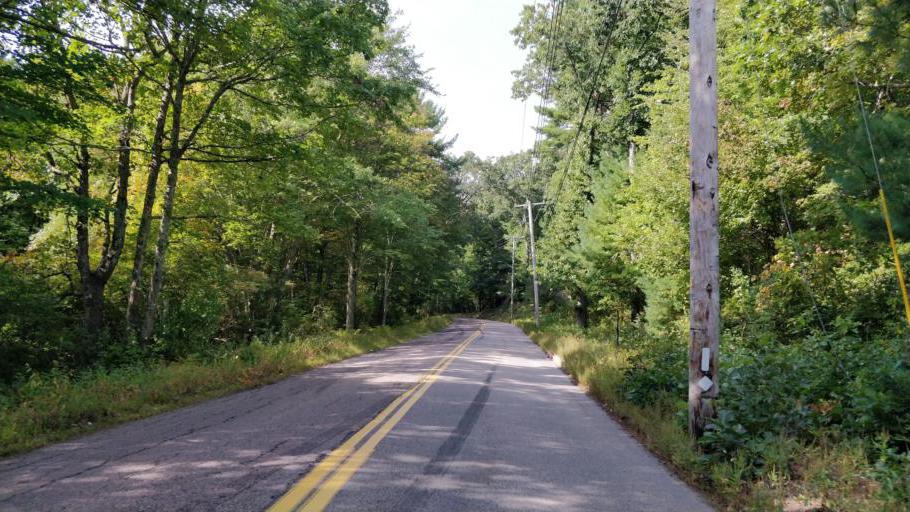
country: US
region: Massachusetts
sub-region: Bristol County
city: Attleboro
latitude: 41.9413
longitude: -71.2400
